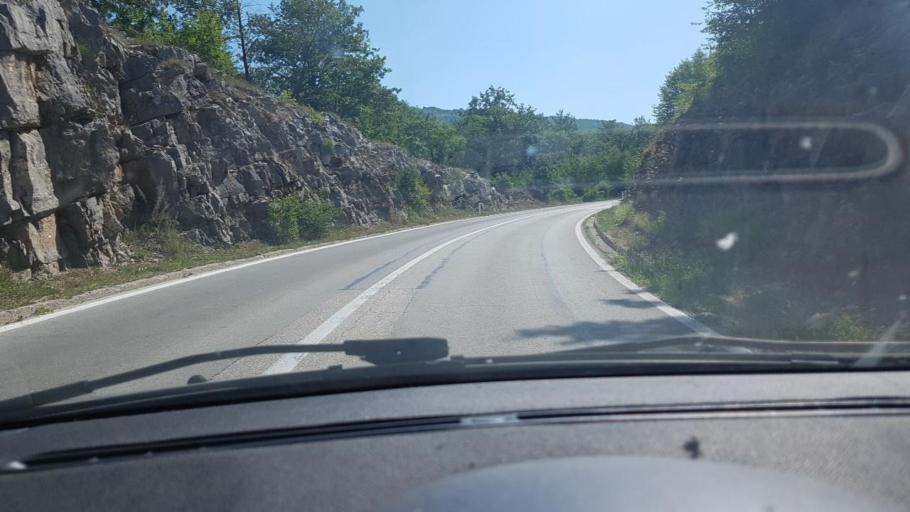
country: BA
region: Federation of Bosnia and Herzegovina
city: Bosansko Grahovo
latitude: 44.3134
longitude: 16.3130
